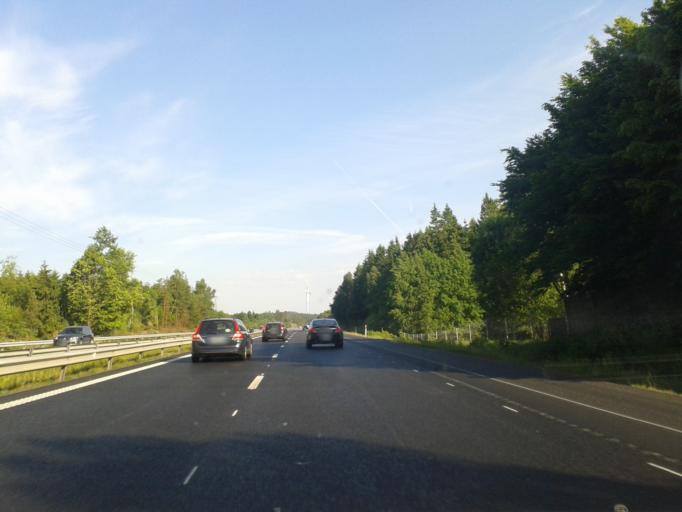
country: SE
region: Vaestra Goetaland
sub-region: Kungalvs Kommun
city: Kode
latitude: 57.9102
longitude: 11.8963
